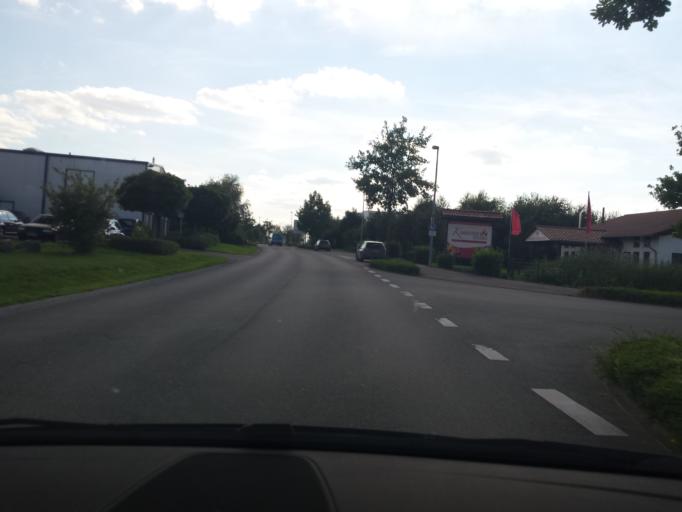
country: DE
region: North Rhine-Westphalia
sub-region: Regierungsbezirk Arnsberg
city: Lippstadt
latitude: 51.6525
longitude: 8.3537
